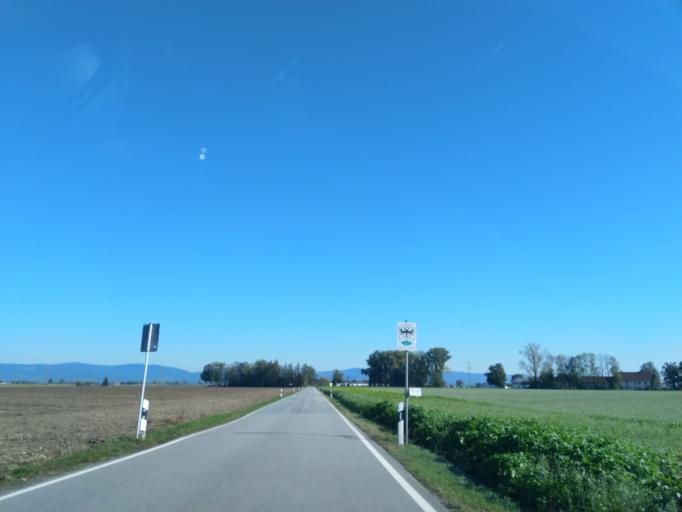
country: DE
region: Bavaria
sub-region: Lower Bavaria
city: Stephansposching
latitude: 48.7902
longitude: 12.7643
